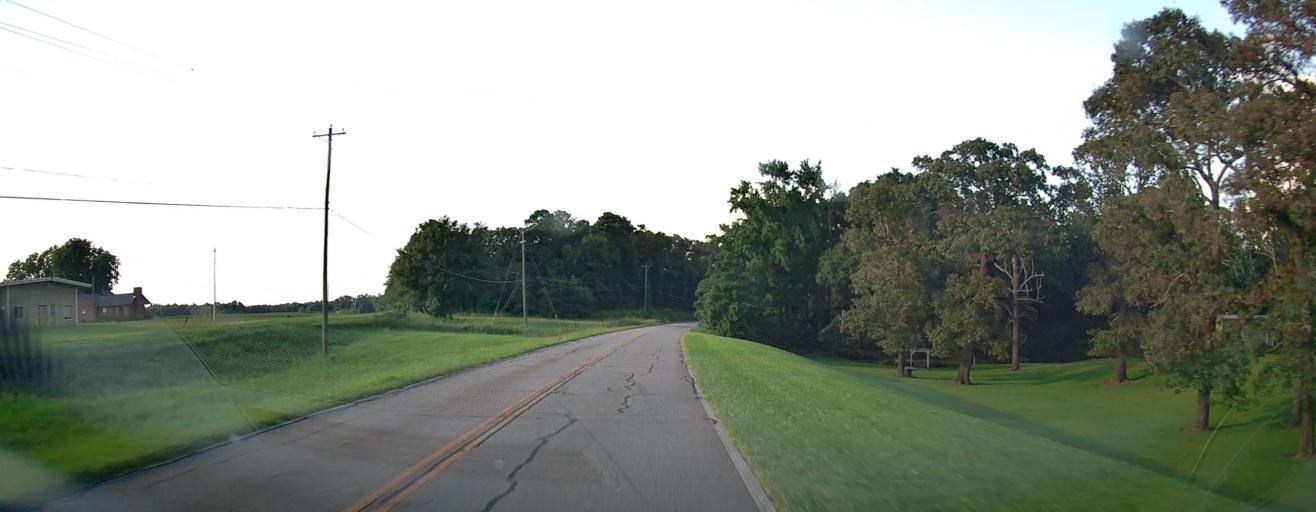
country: US
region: Georgia
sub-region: Peach County
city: Fort Valley
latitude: 32.6114
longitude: -83.8337
